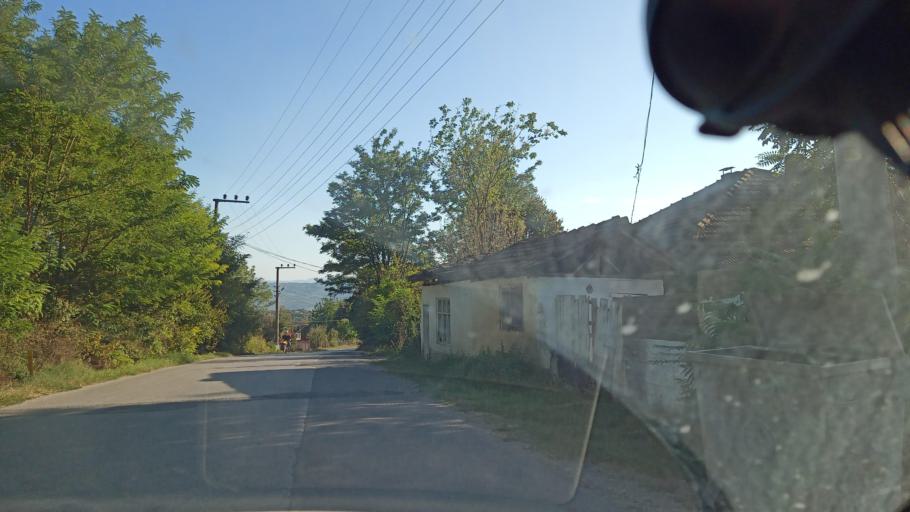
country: TR
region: Sakarya
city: Kazimpasa
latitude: 40.8531
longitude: 30.2820
